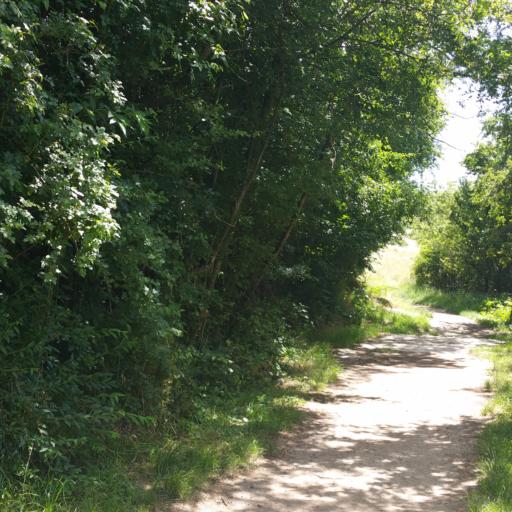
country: AT
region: Lower Austria
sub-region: Politischer Bezirk Modling
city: Perchtoldsdorf
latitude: 48.2121
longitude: 16.2717
